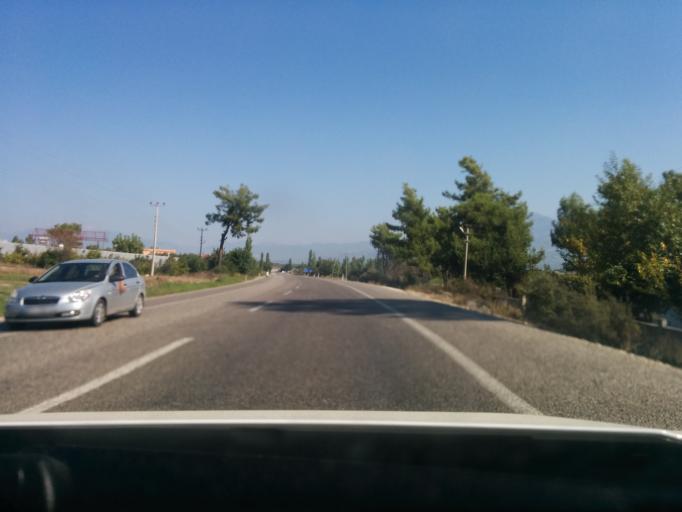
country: TR
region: Mugla
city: Esen
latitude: 36.5139
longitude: 29.3364
